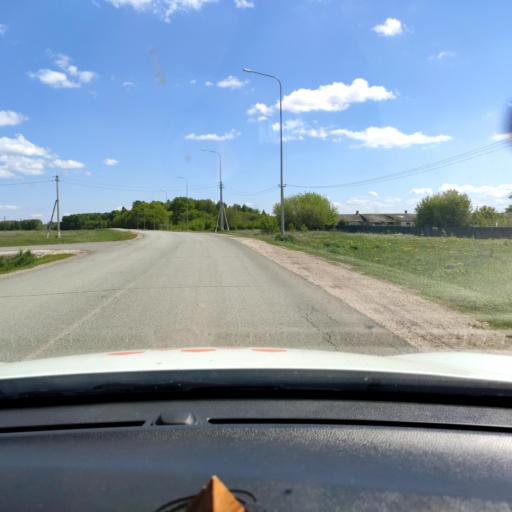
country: RU
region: Tatarstan
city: Kuybyshevskiy Zaton
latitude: 55.1601
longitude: 49.1831
